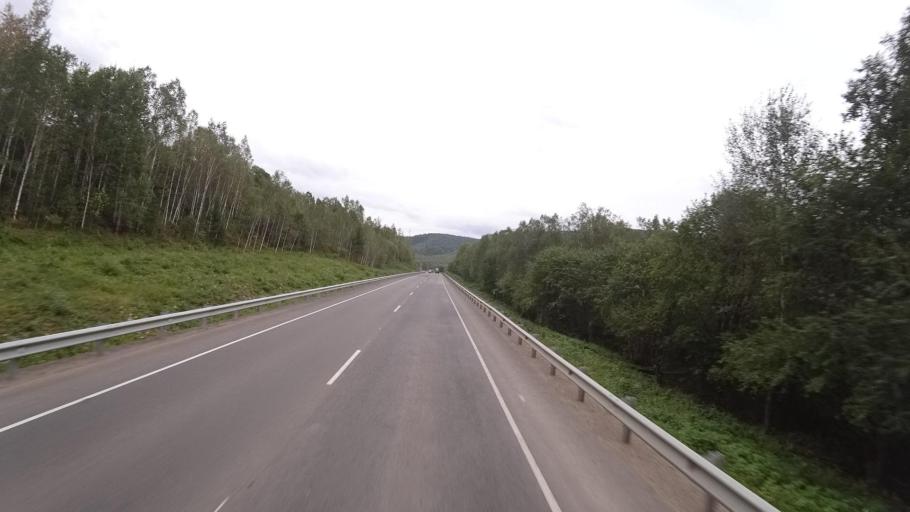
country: RU
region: Jewish Autonomous Oblast
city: Khingansk
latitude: 48.9849
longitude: 131.1424
